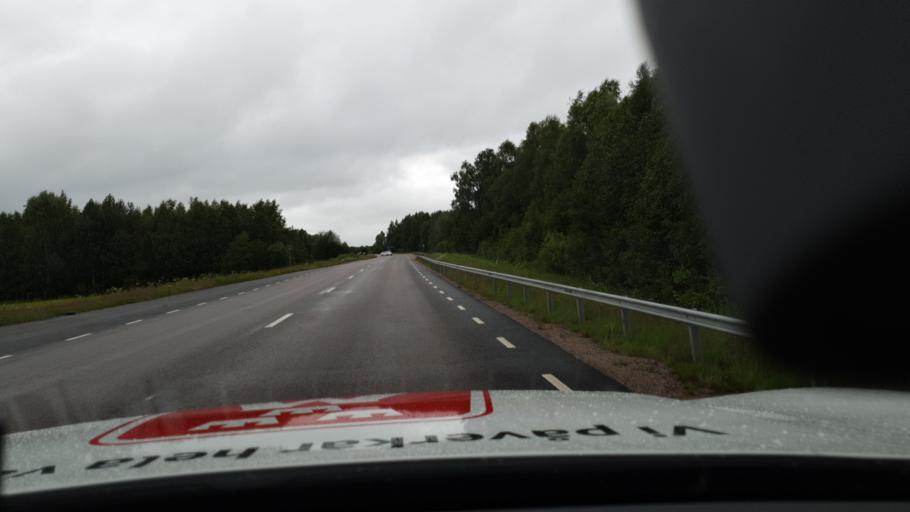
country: SE
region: Norrbotten
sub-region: Overtornea Kommun
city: OEvertornea
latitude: 66.4180
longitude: 23.6265
